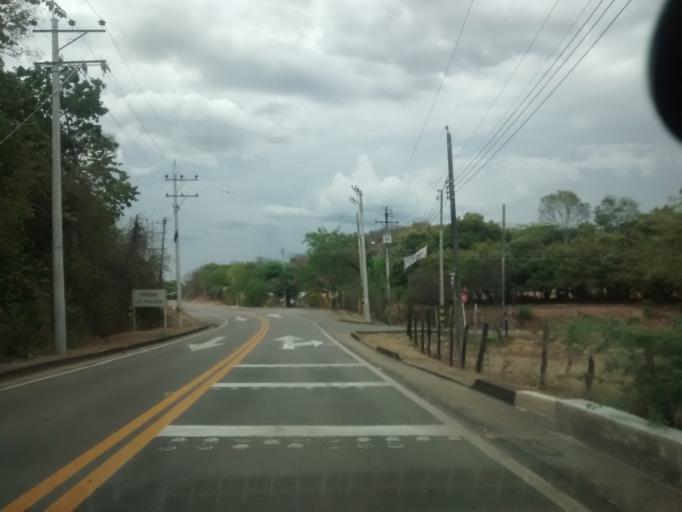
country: CO
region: Cundinamarca
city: Agua de Dios
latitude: 4.4263
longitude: -74.6984
